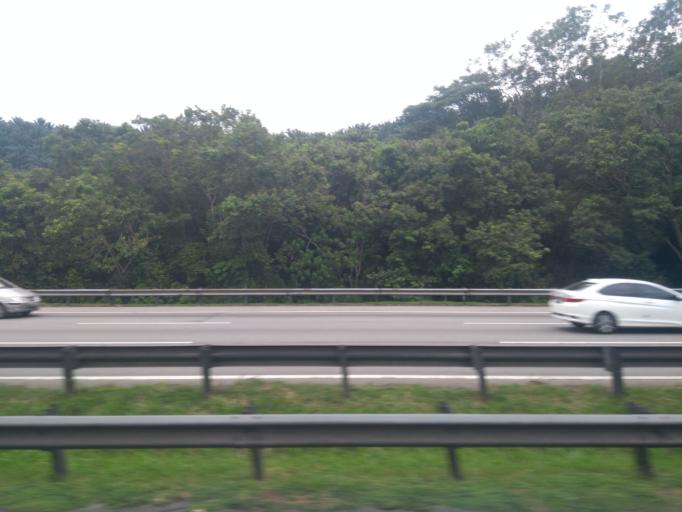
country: MY
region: Negeri Sembilan
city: Tampin
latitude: 2.4644
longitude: 102.1571
